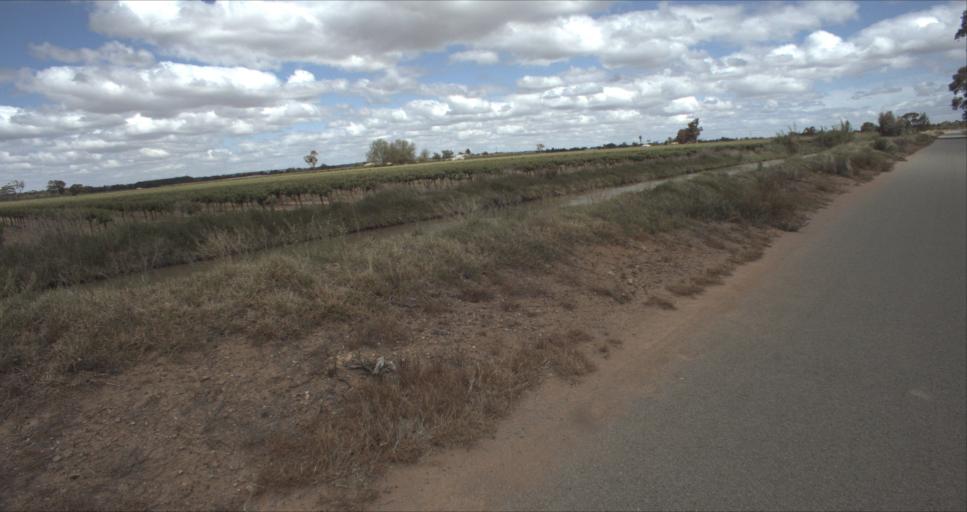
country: AU
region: New South Wales
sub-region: Leeton
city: Leeton
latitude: -34.5743
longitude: 146.3985
